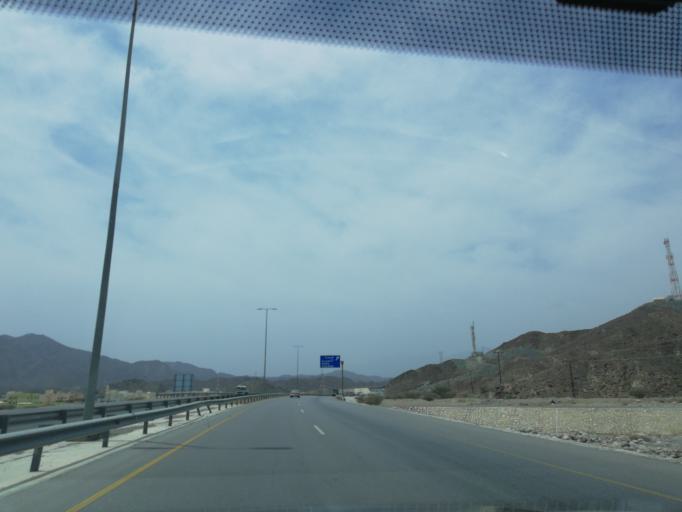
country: OM
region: Muhafazat ad Dakhiliyah
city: Sufalat Sama'il
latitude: 23.3742
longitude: 58.0486
